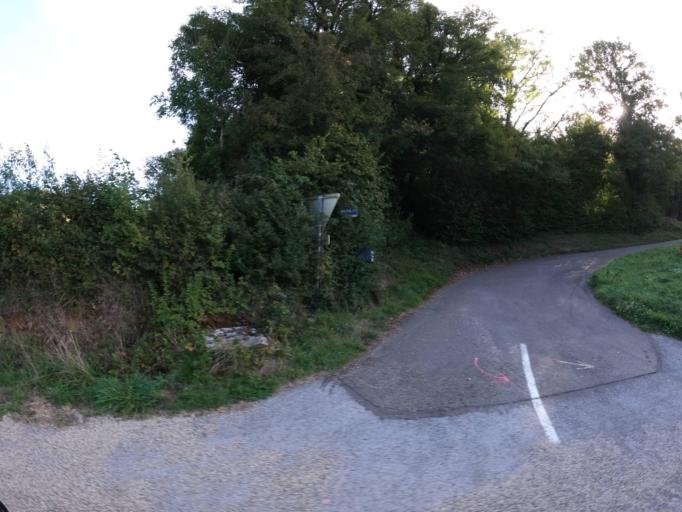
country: FR
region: Franche-Comte
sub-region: Departement du Jura
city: Montmorot
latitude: 46.7057
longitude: 5.5288
